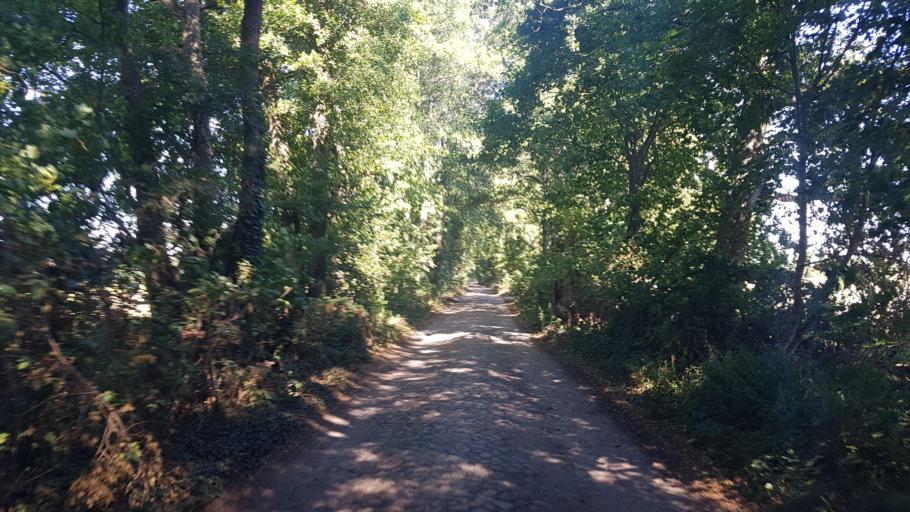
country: DE
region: Brandenburg
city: Brandenburg an der Havel
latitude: 52.3396
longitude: 12.5384
